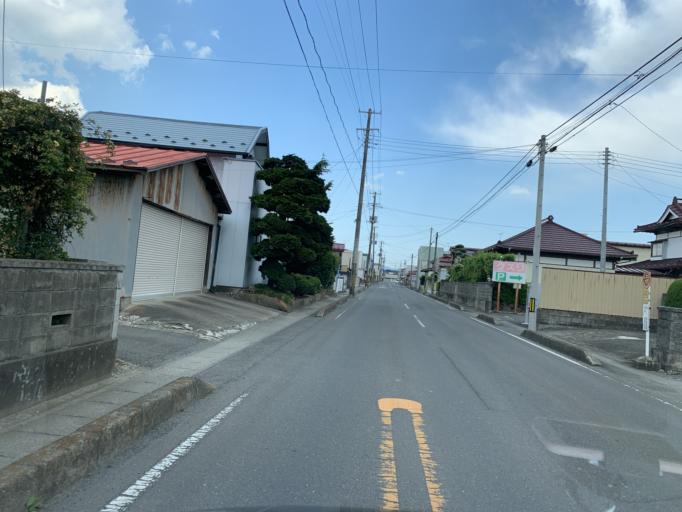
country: JP
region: Miyagi
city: Wakuya
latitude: 38.6298
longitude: 141.1959
